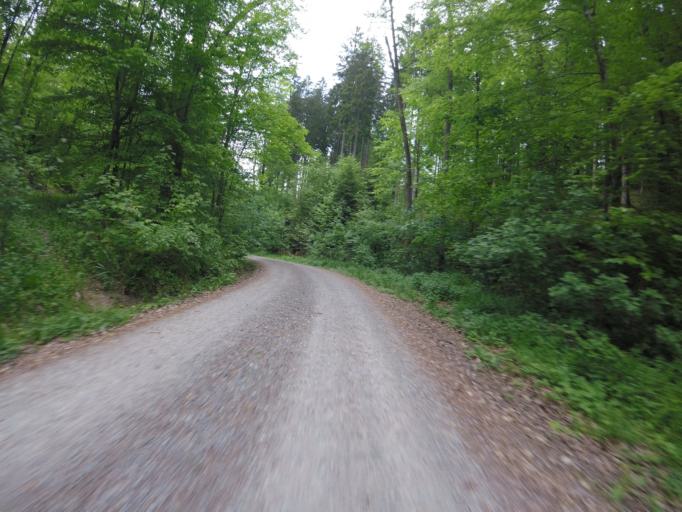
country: DE
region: Baden-Wuerttemberg
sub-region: Regierungsbezirk Stuttgart
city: Spiegelberg
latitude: 49.0124
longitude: 9.4353
